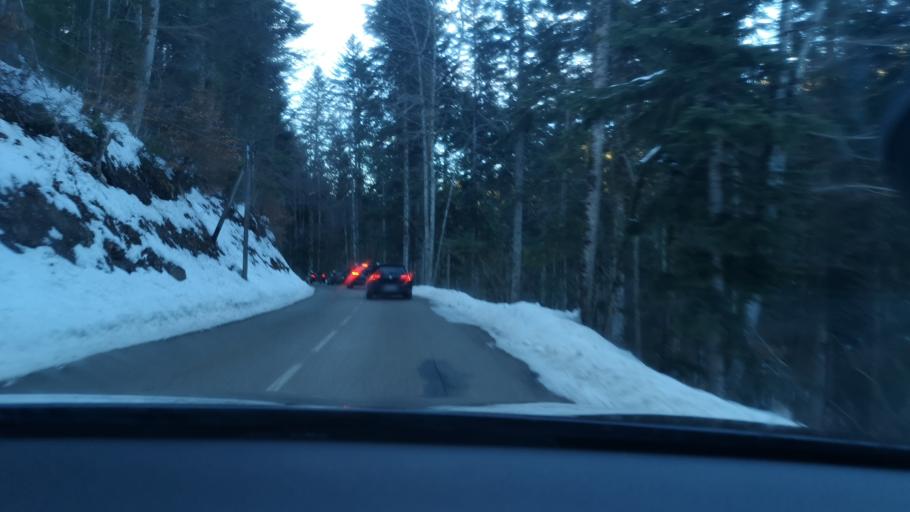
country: FR
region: Franche-Comte
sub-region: Departement du Doubs
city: Montlebon
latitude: 46.9844
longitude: 6.5540
